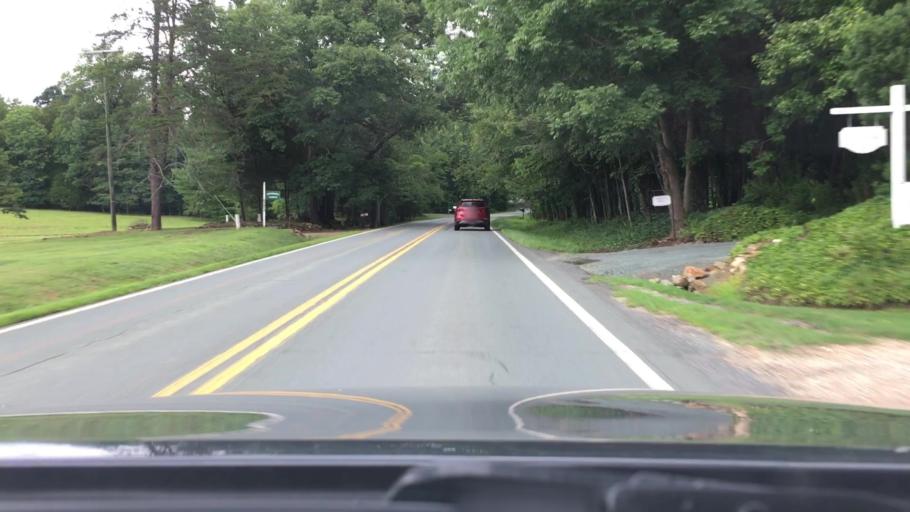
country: US
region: Virginia
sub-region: Fluvanna County
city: Lake Monticello
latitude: 38.0583
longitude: -78.3133
